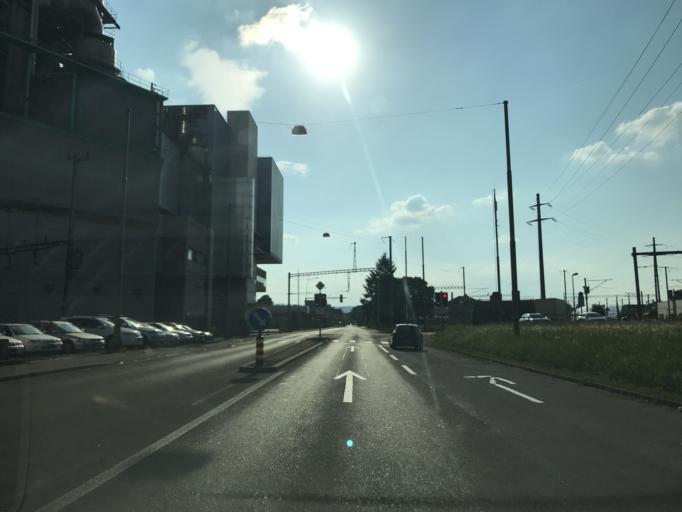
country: CH
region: Zurich
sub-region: Bezirk Winterthur
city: Mattenbach (Kreis 7) / Gutschick
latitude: 47.4985
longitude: 8.7539
